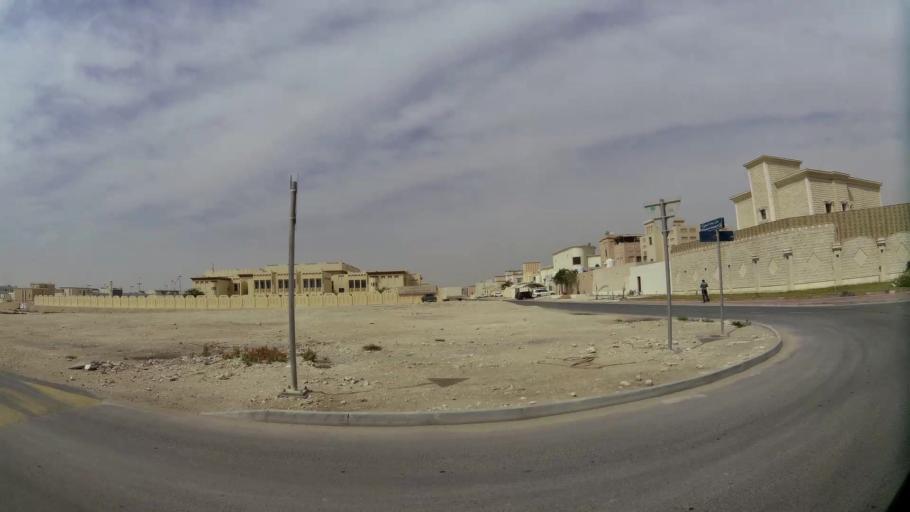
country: QA
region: Baladiyat ad Dawhah
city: Doha
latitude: 25.2119
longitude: 51.4892
